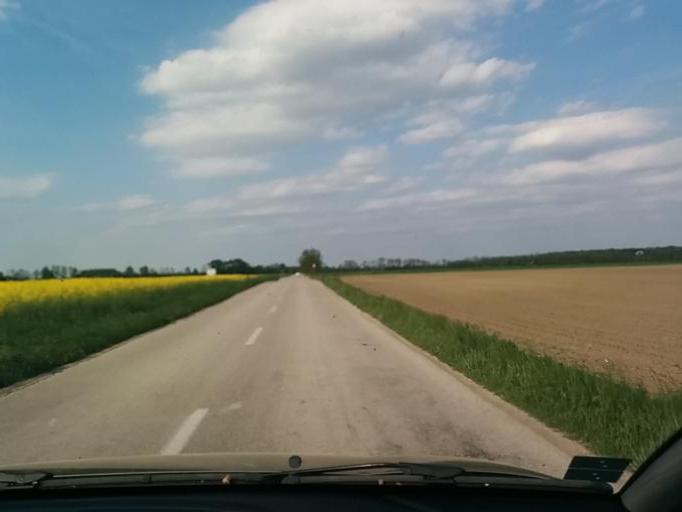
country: SK
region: Trnavsky
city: Sladkovicovo
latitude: 48.2101
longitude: 17.5452
